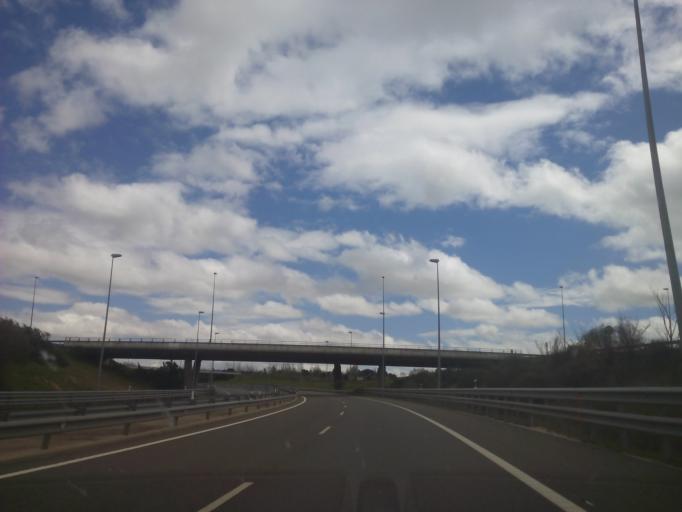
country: ES
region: Castille and Leon
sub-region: Provincia de Salamanca
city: Carbajosa de la Sagrada
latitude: 40.9445
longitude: -5.6429
